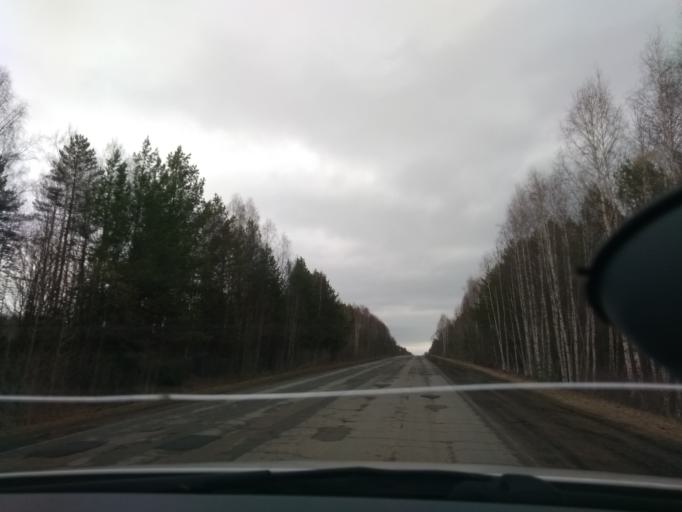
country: RU
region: Perm
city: Kungur
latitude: 57.3579
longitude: 56.8117
